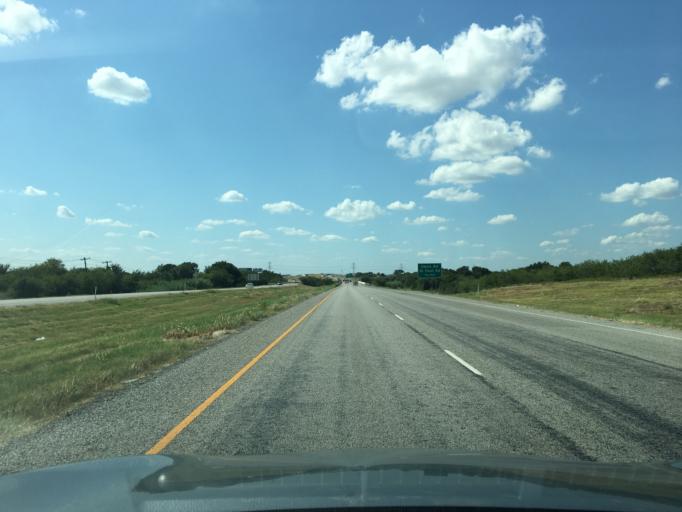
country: US
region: Texas
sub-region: Ellis County
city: Midlothian
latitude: 32.5111
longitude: -97.0647
